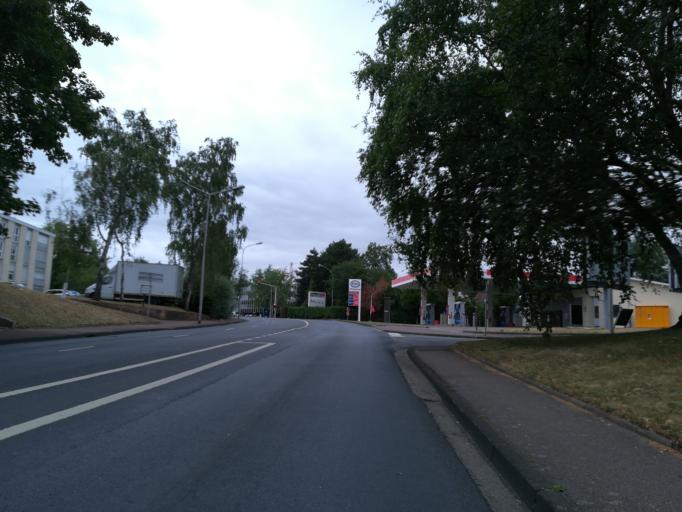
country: FR
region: Haute-Normandie
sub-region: Departement de la Seine-Maritime
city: Mont-Saint-Aignan
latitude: 49.4601
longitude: 1.0827
